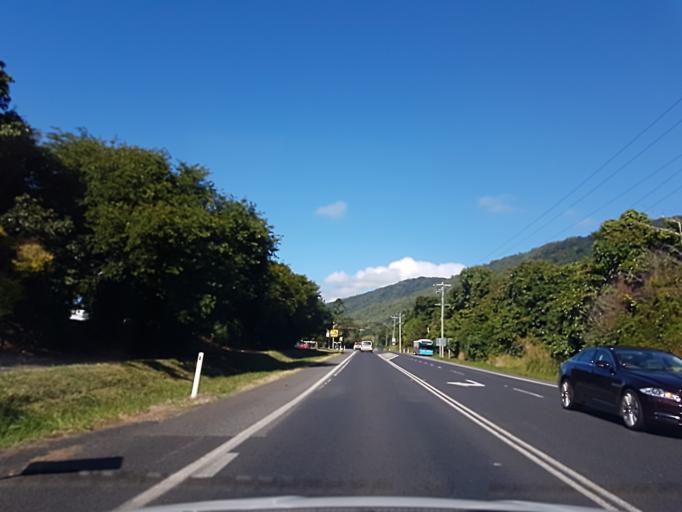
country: AU
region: Queensland
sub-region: Cairns
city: Palm Cove
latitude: -16.7462
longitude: 145.6634
